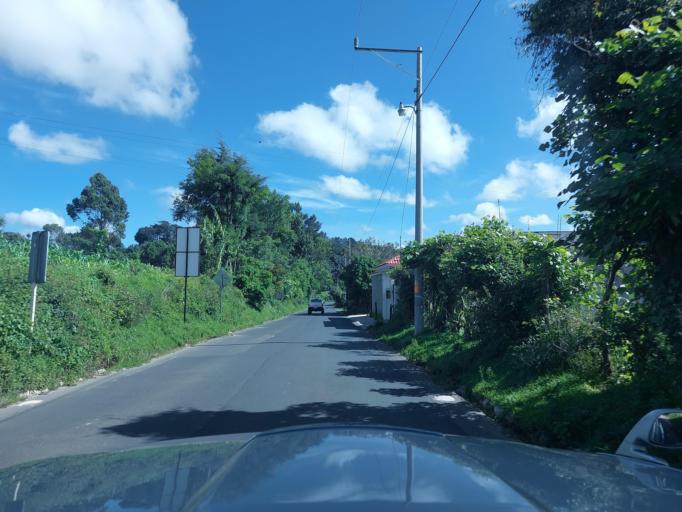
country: GT
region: Chimaltenango
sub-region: Municipio de Zaragoza
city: Zaragoza
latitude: 14.6496
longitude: -90.8973
